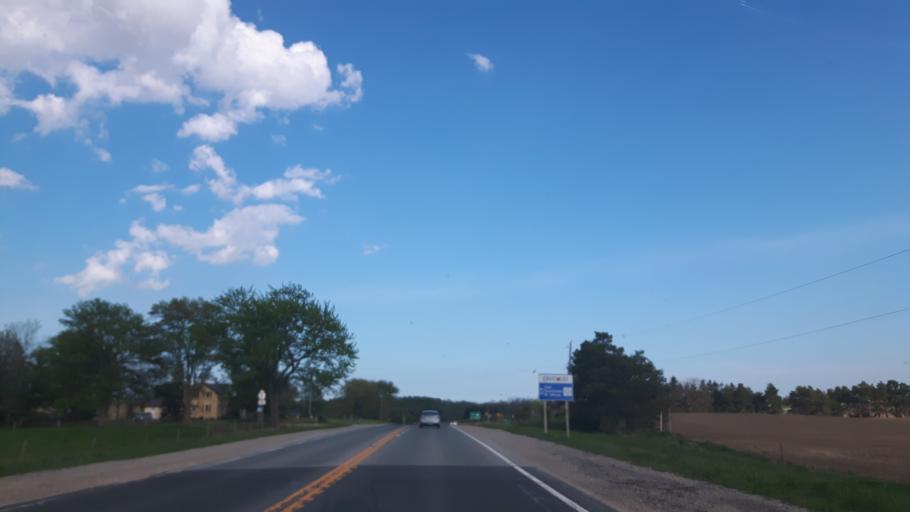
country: CA
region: Ontario
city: South Huron
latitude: 43.1684
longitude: -81.3594
